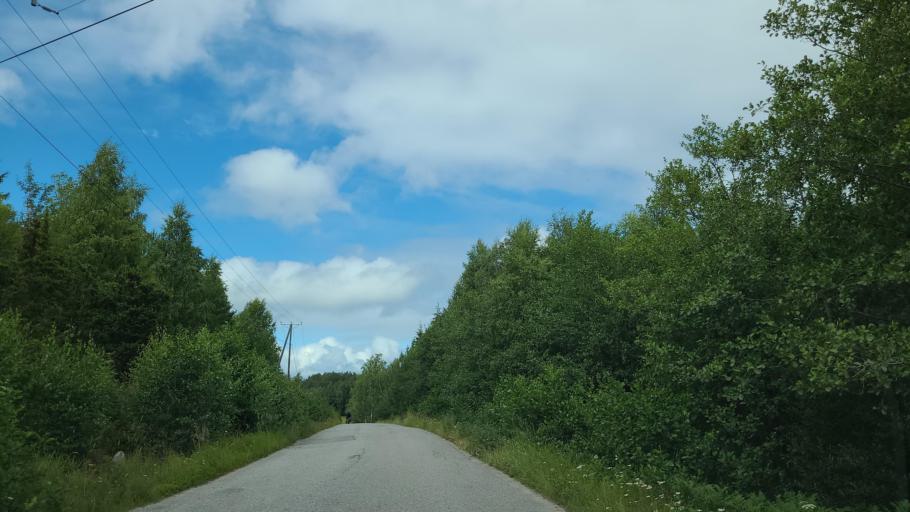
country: FI
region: Varsinais-Suomi
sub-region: Aboland-Turunmaa
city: Nagu
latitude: 60.1709
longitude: 21.9810
